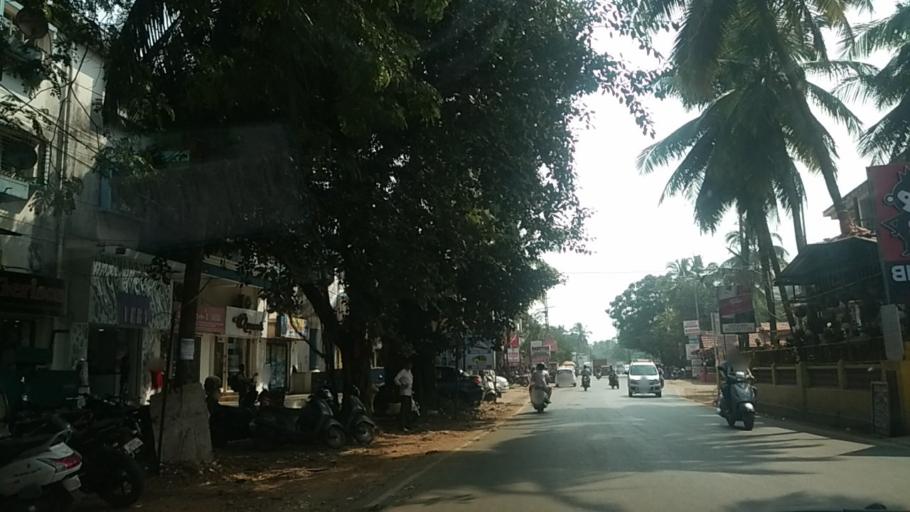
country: IN
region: Goa
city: Calangute
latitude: 15.5353
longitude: 73.7643
